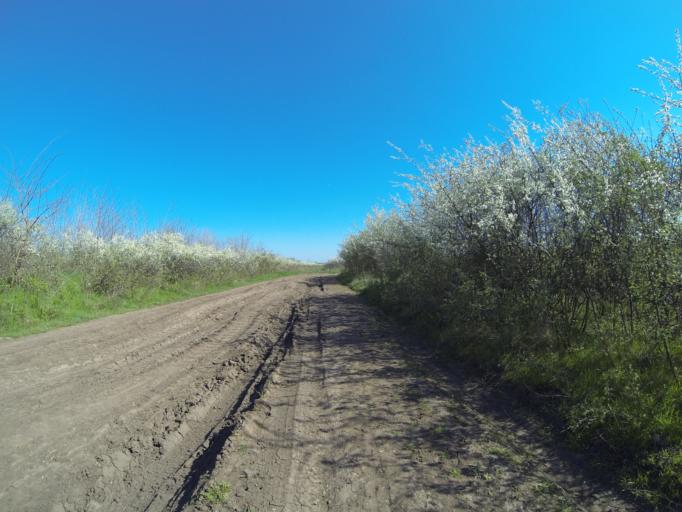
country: RO
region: Dolj
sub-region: Comuna Intorsura
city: Intorsura
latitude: 44.1336
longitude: 23.5941
